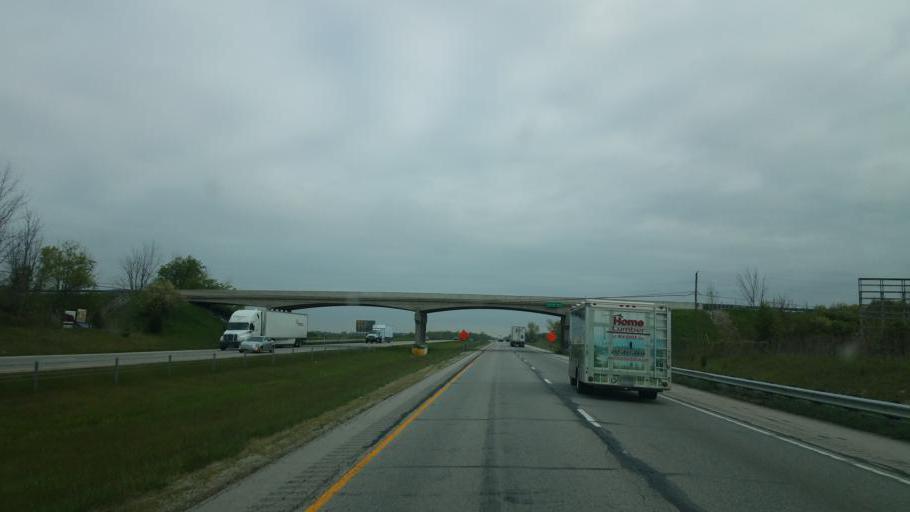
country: US
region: Indiana
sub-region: DeKalb County
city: Garrett
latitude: 41.2789
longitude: -85.0869
